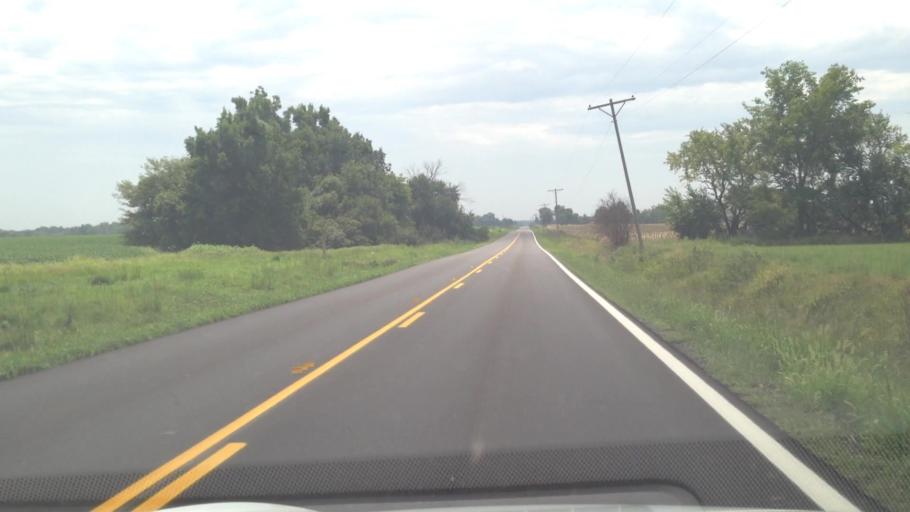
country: US
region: Kansas
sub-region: Crawford County
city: Girard
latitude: 37.6353
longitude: -94.9698
